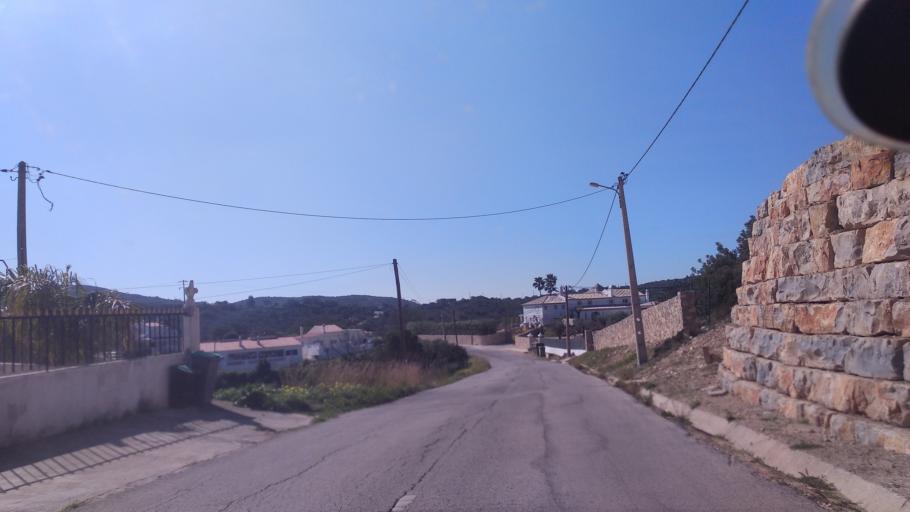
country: PT
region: Faro
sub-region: Faro
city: Santa Barbara de Nexe
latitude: 37.1126
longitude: -7.9328
